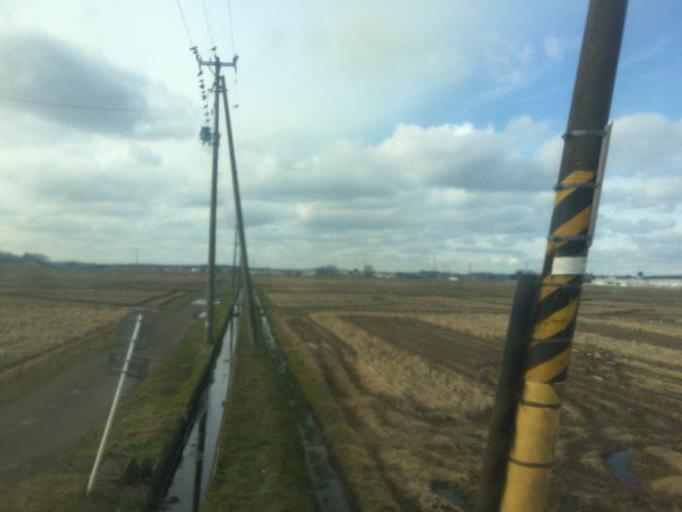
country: JP
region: Akita
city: Noshiromachi
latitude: 40.1790
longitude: 140.0587
